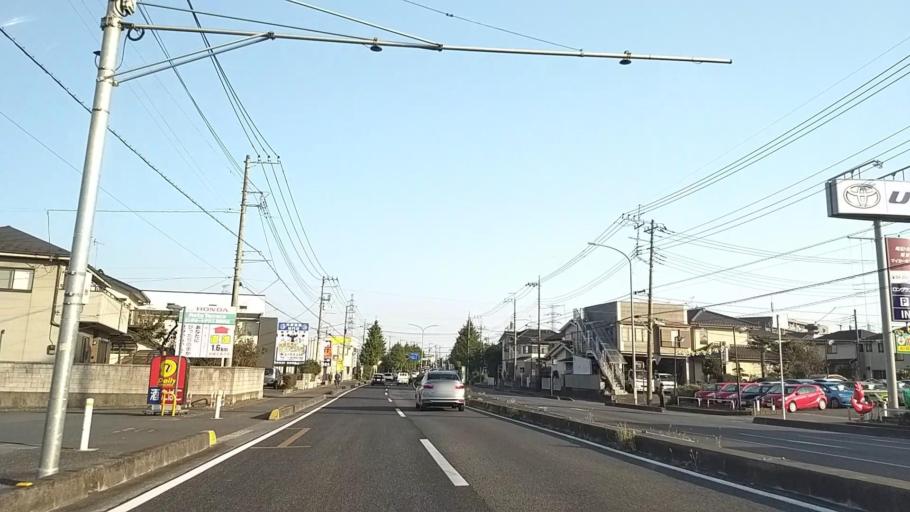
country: JP
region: Saitama
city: Tokorozawa
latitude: 35.7937
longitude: 139.4401
